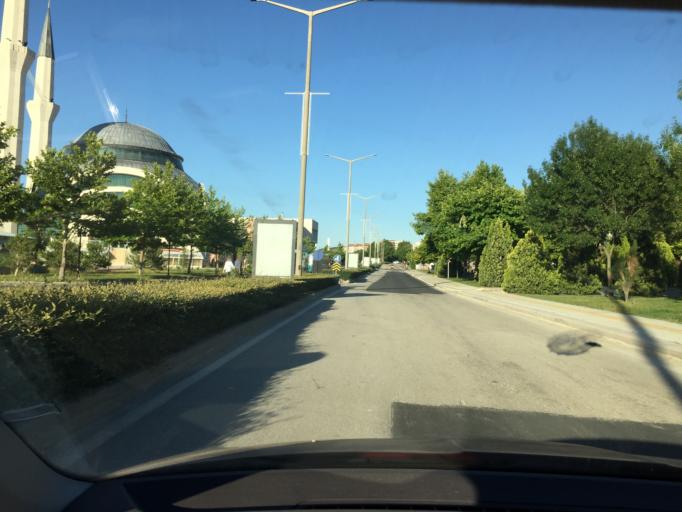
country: TR
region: Eskisehir
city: Eskisehir
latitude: 39.7530
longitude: 30.4842
